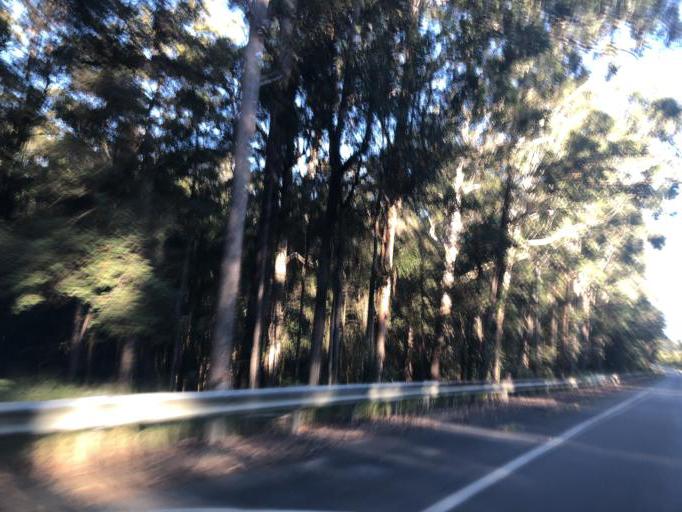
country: AU
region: New South Wales
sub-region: Nambucca Shire
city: Nambucca
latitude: -30.5544
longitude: 153.0067
